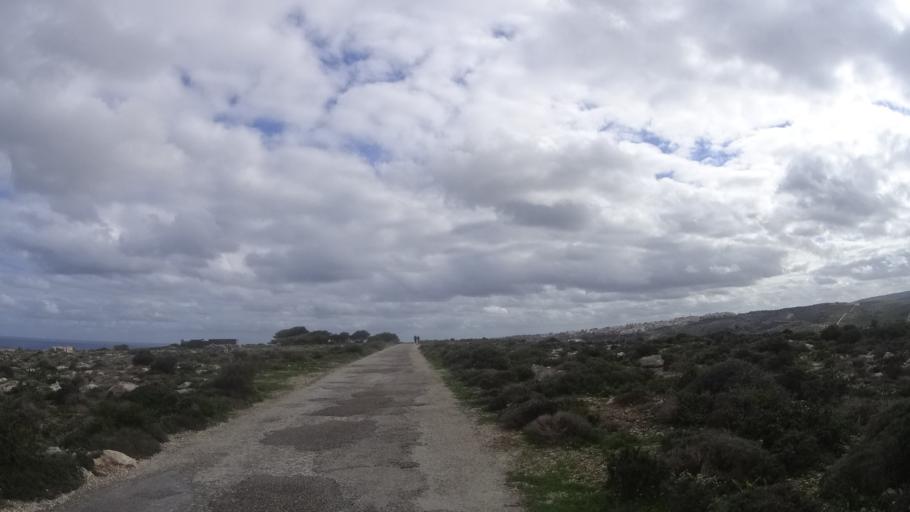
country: MT
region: Il-Mellieha
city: Mellieha
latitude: 35.9725
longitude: 14.3321
